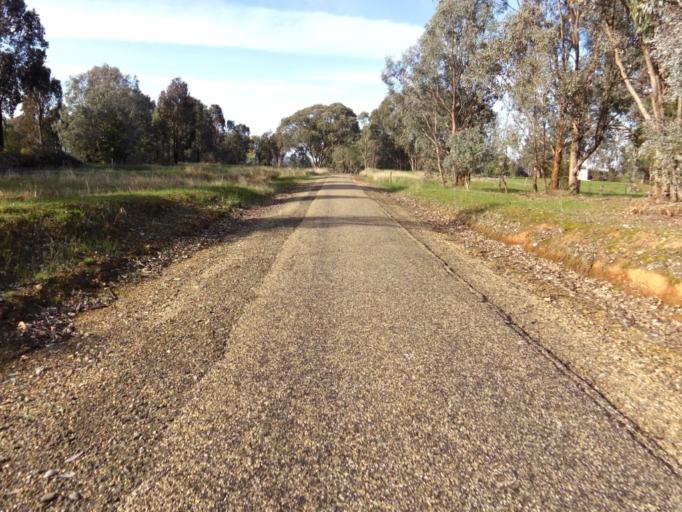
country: AU
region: Victoria
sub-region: Wangaratta
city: Wangaratta
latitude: -36.4128
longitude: 146.5497
